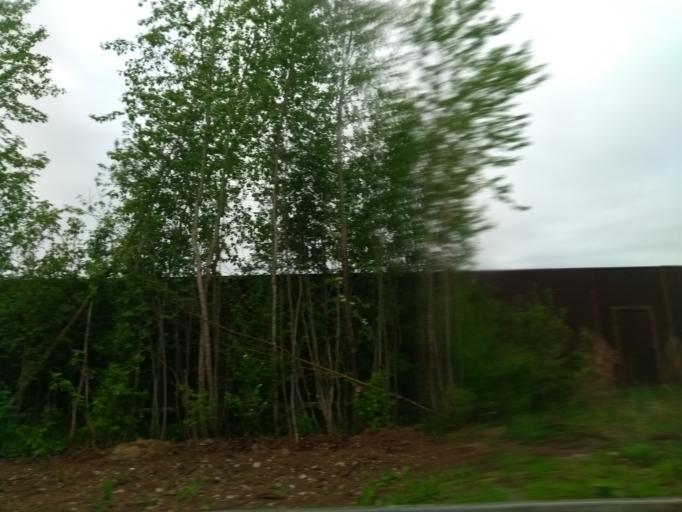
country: RU
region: Perm
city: Perm
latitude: 58.0014
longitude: 56.3357
